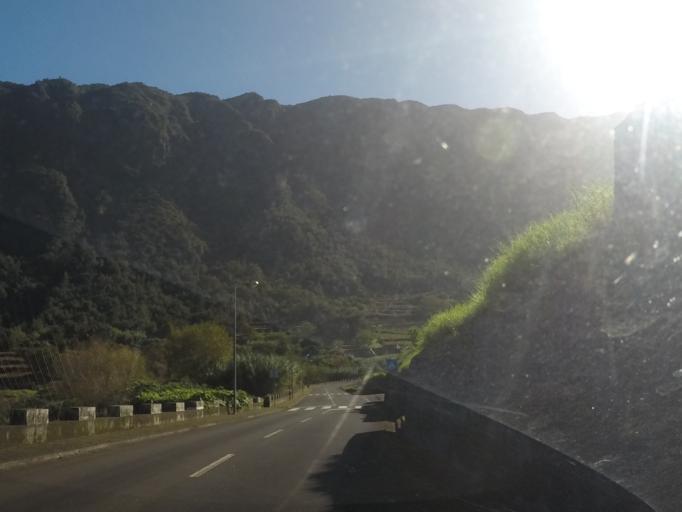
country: PT
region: Madeira
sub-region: Santana
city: Santana
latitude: 32.8029
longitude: -16.9614
